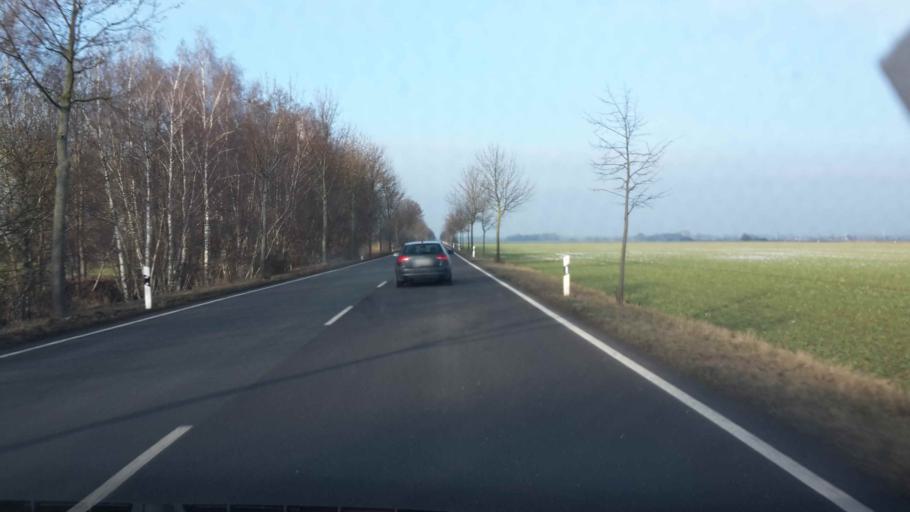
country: DE
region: Saxony-Anhalt
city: Seehausen
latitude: 52.9175
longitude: 11.7336
